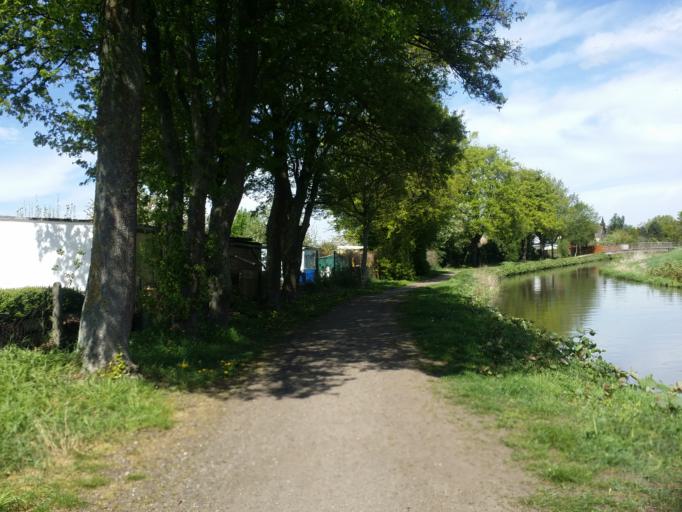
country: DE
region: Lower Saxony
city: Delmenhorst
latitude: 53.0652
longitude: 8.6547
